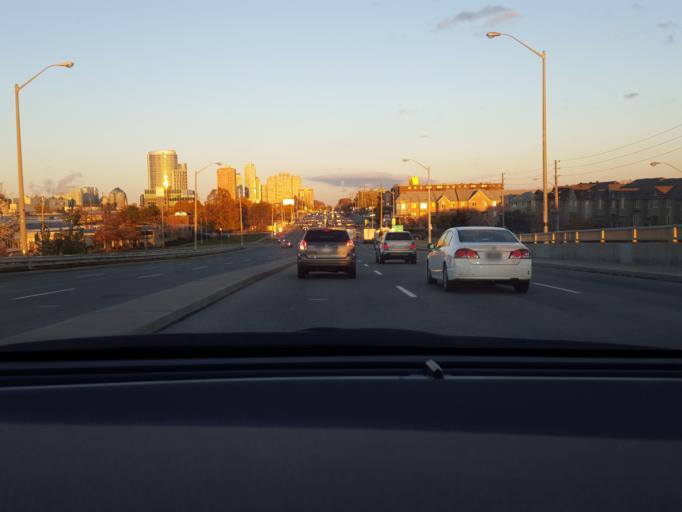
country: CA
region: Ontario
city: Scarborough
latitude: 43.7671
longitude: -79.2748
